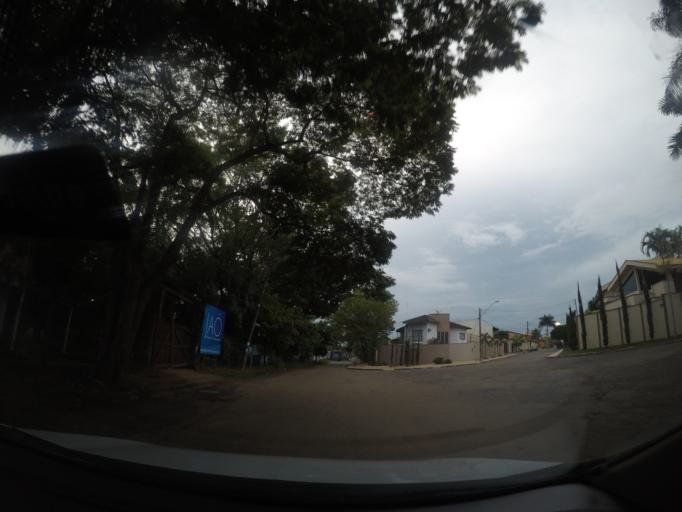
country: BR
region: Goias
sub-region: Goiania
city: Goiania
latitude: -16.6538
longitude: -49.2260
